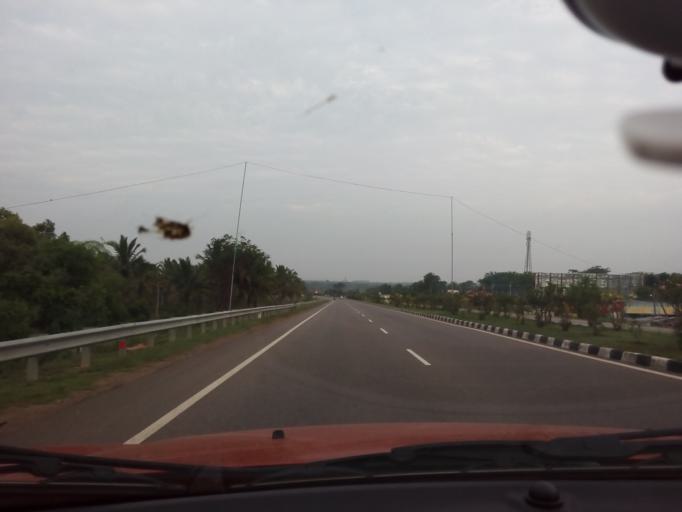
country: IN
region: Karnataka
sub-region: Tumkur
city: Kunigal
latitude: 12.9970
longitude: 76.9158
